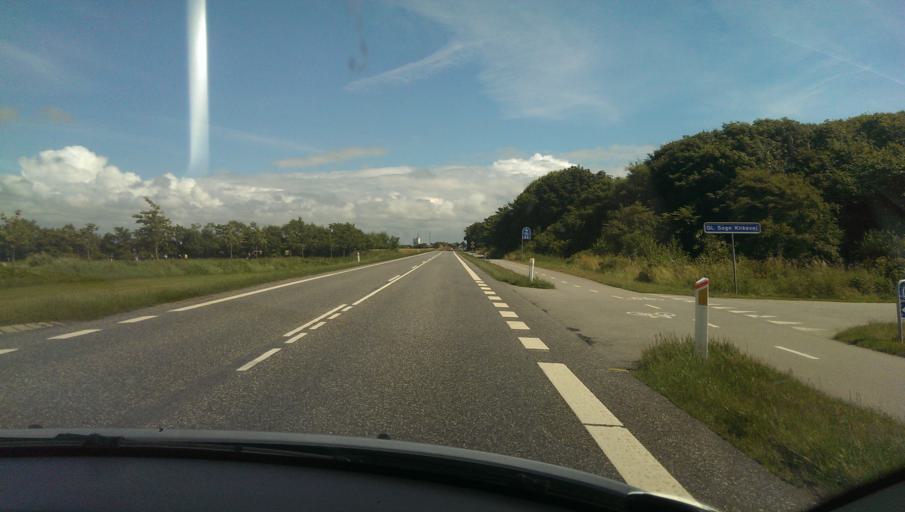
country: DK
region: Central Jutland
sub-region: Ringkobing-Skjern Kommune
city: Ringkobing
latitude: 56.1053
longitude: 8.2100
